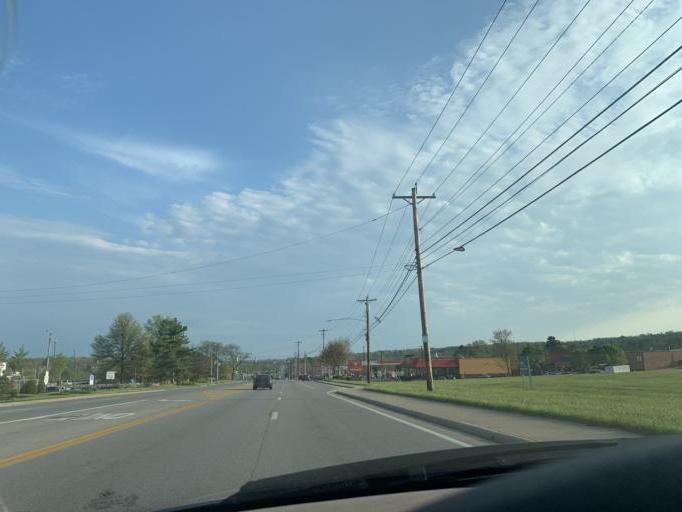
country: US
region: Ohio
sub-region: Hamilton County
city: Woodlawn
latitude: 39.2620
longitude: -84.4695
